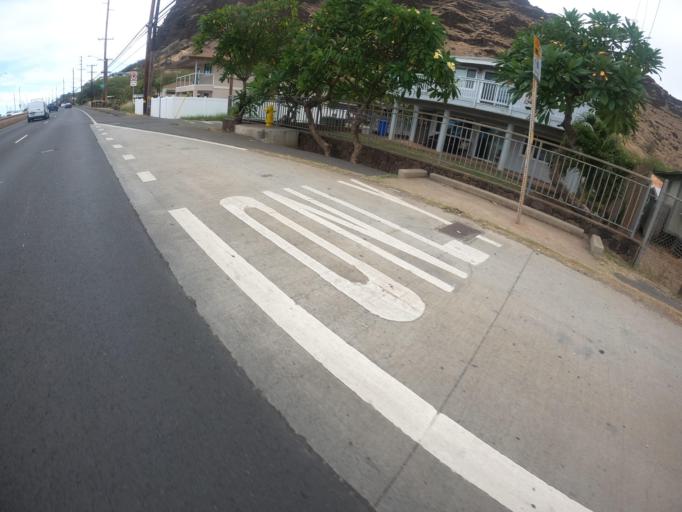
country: US
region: Hawaii
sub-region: Honolulu County
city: Nanakuli
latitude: 21.3976
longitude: -158.1657
